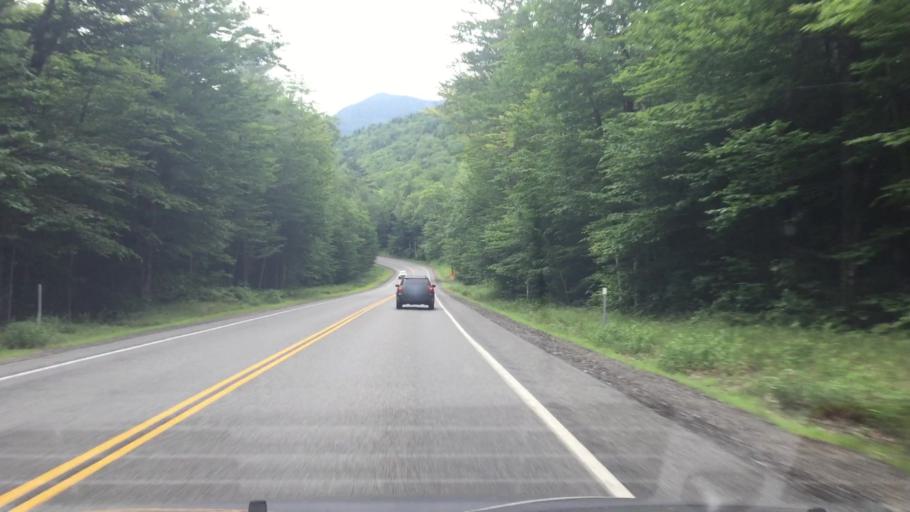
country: US
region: New Hampshire
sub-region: Carroll County
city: North Conway
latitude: 44.0820
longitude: -71.3469
